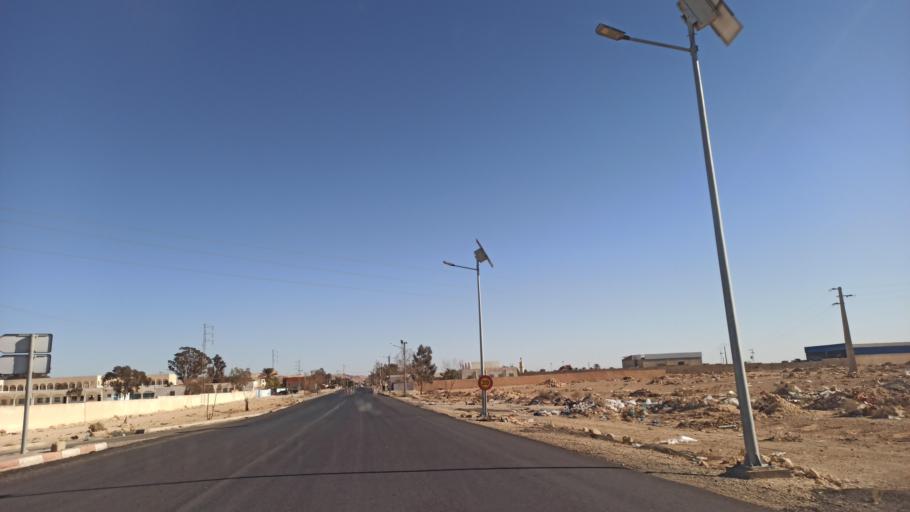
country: TN
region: Gafsa
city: Al Metlaoui
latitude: 34.3093
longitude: 8.3772
